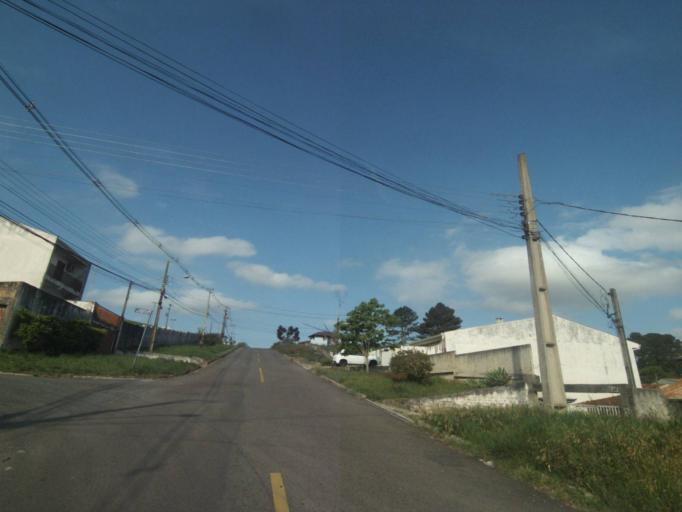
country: BR
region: Parana
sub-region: Pinhais
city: Pinhais
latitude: -25.4097
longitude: -49.2111
